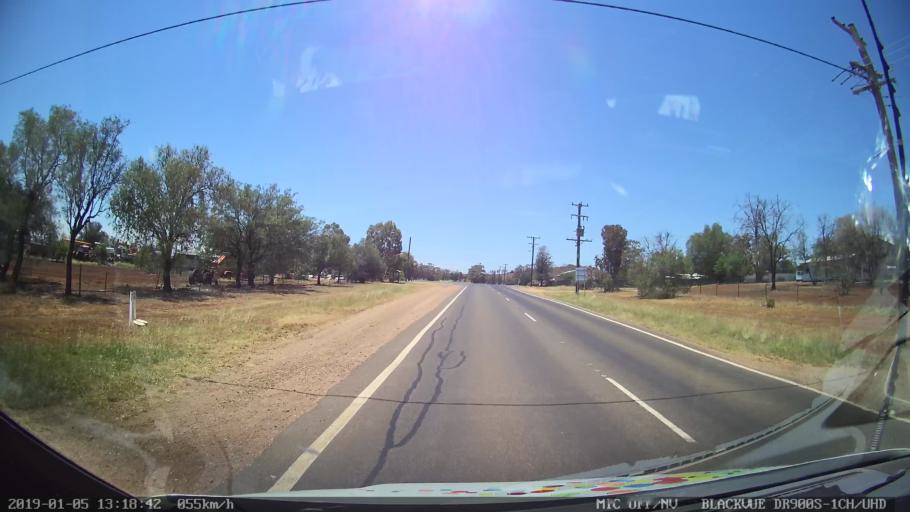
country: AU
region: New South Wales
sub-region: Gunnedah
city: Gunnedah
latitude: -31.0967
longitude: 149.9126
